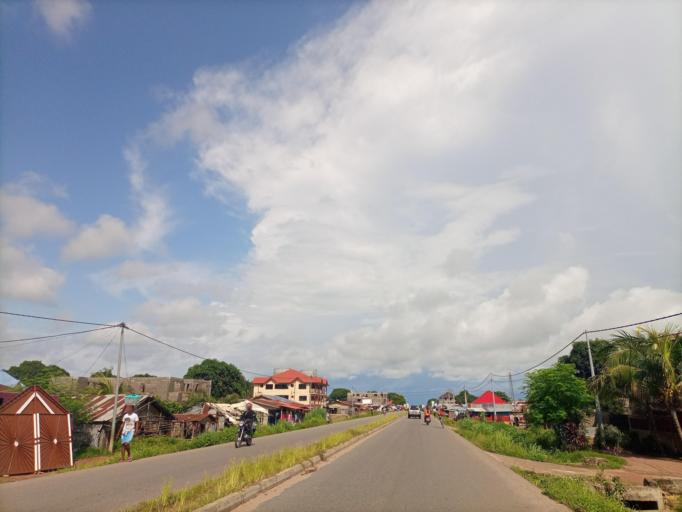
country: SL
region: Northern Province
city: Masoyila
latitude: 8.6060
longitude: -13.1821
